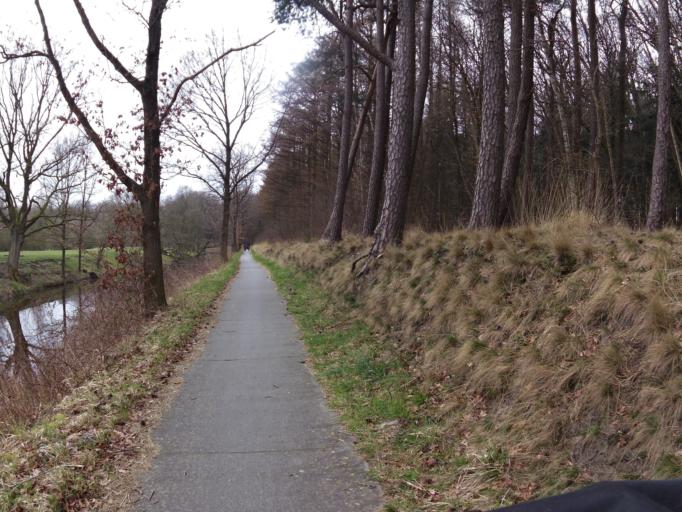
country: NL
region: Drenthe
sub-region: Gemeente Westerveld
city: Dwingeloo
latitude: 52.9713
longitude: 6.3825
